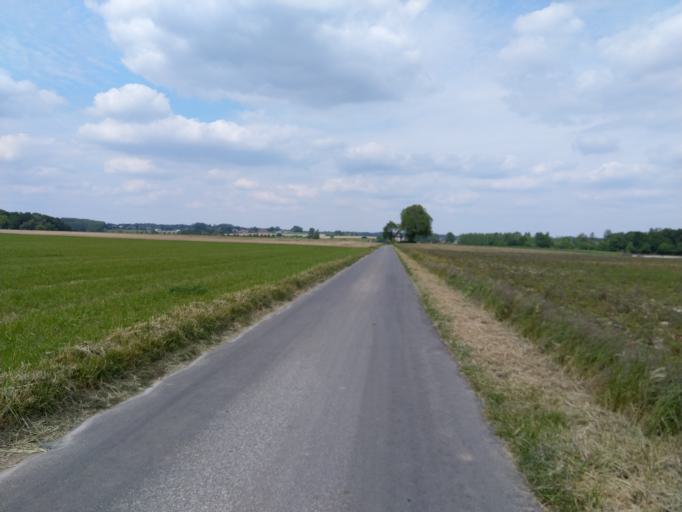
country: BE
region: Wallonia
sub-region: Province du Hainaut
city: Lens
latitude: 50.5915
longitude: 3.9489
